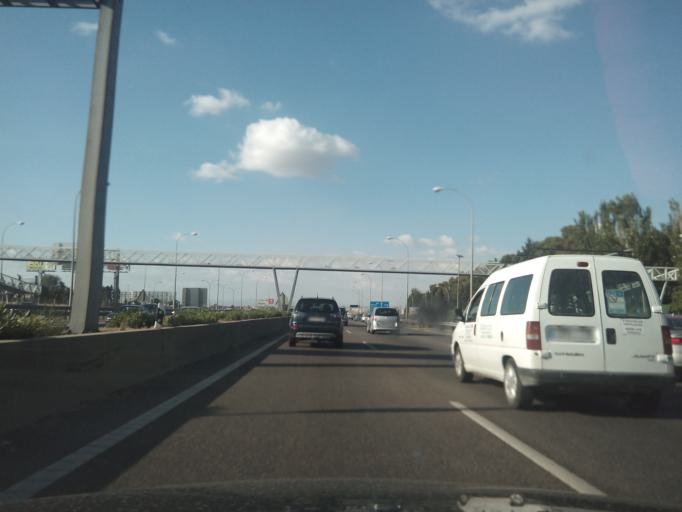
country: ES
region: Madrid
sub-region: Provincia de Madrid
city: Las Tablas
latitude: 40.5214
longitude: -3.6517
